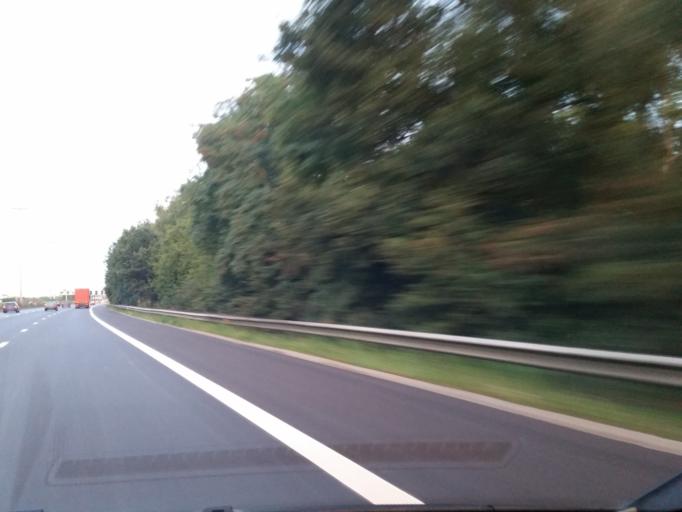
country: BE
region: Flanders
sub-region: Provincie Oost-Vlaanderen
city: Melle
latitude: 50.9957
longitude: 3.7830
